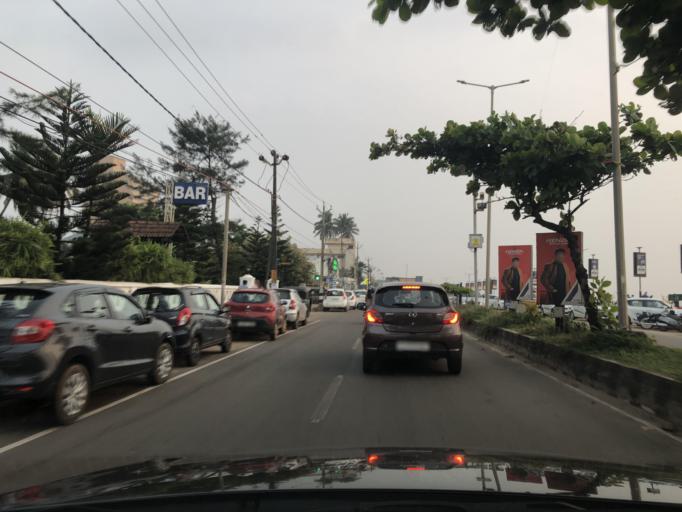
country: IN
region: Kerala
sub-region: Kozhikode
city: Kozhikode
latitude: 11.2530
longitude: 75.7709
